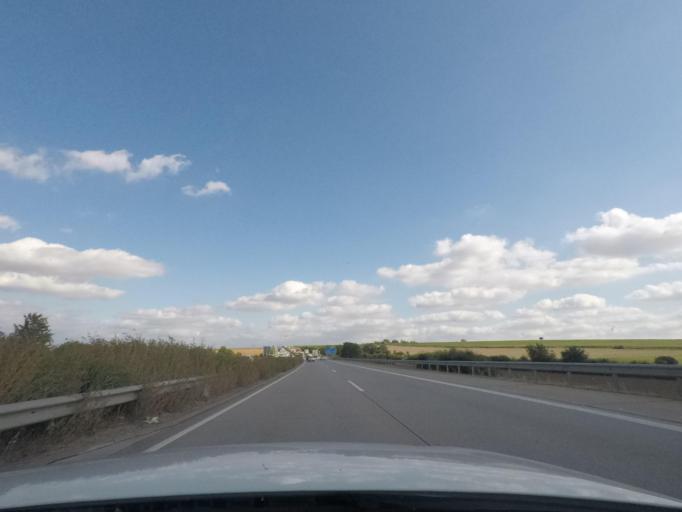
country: DE
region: Rheinland-Pfalz
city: Bissersheim
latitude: 49.5513
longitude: 8.1943
